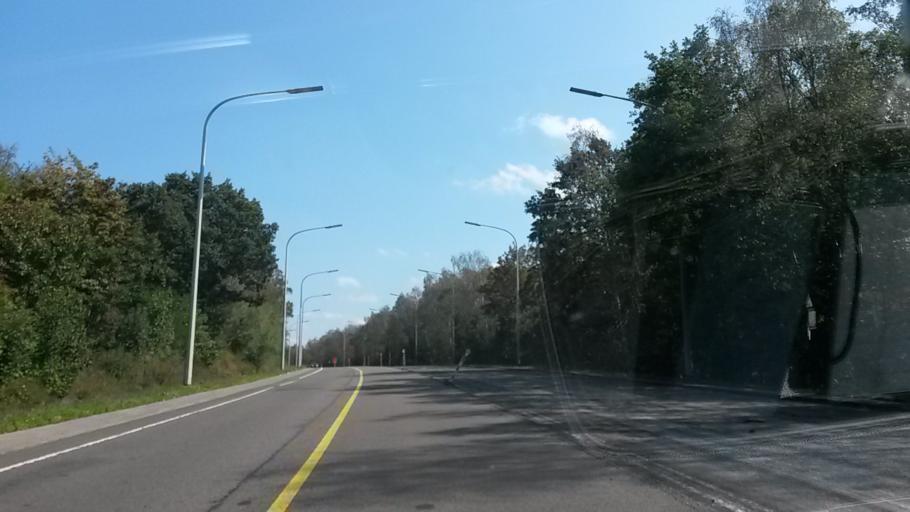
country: BE
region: Wallonia
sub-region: Province du Hainaut
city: Aiseau
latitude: 50.4440
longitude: 4.5766
